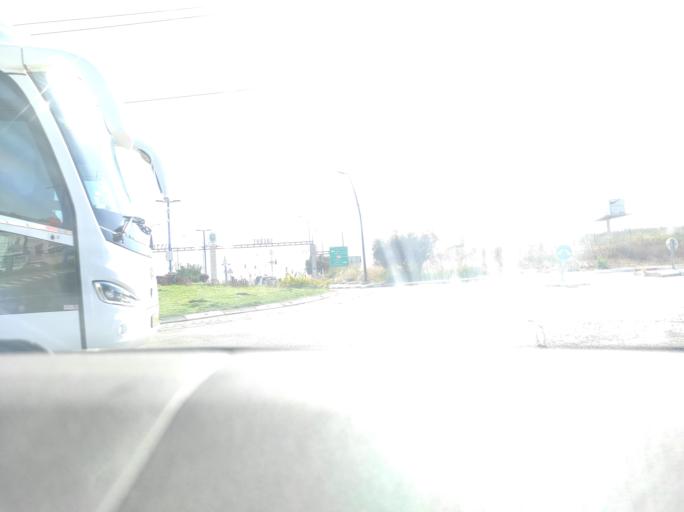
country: IL
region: Southern District
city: Sederot
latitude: 31.5174
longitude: 34.5881
